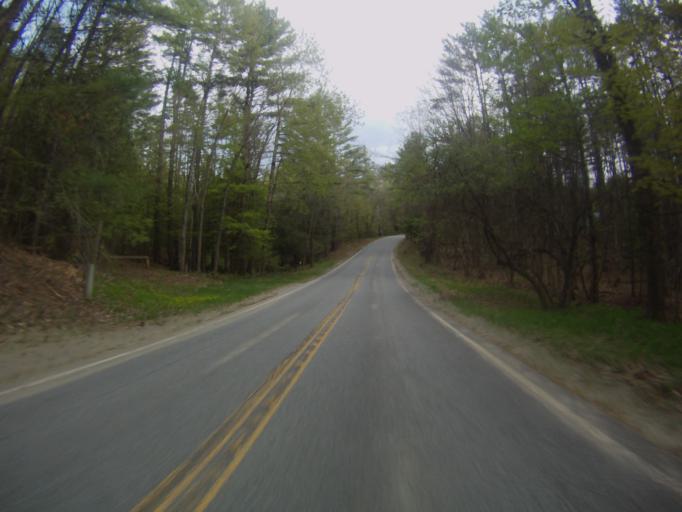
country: US
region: New York
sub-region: Warren County
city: Warrensburg
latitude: 43.7882
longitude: -73.9360
